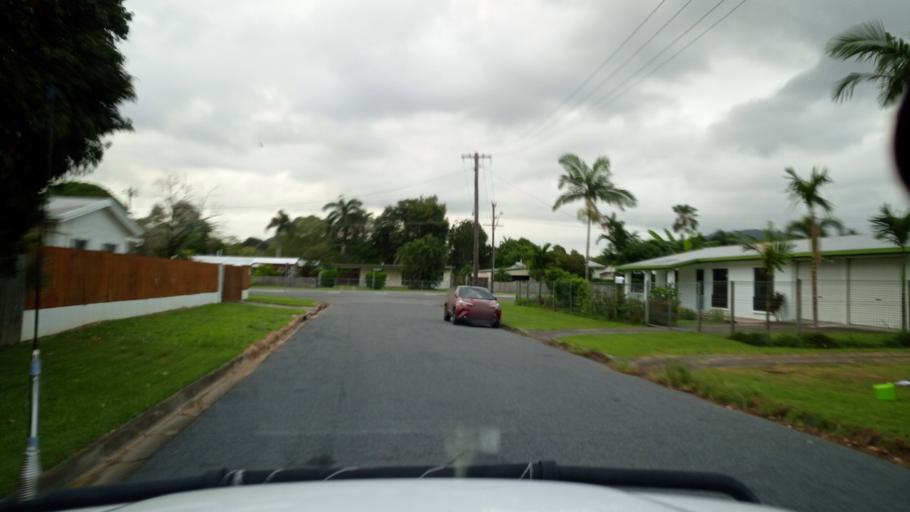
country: AU
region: Queensland
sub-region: Cairns
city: Woree
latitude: -16.9308
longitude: 145.7397
